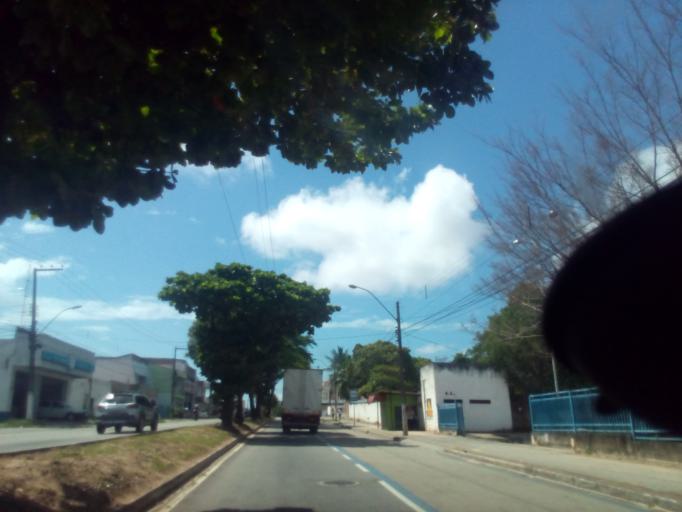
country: BR
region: Rio Grande do Norte
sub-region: Natal
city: Natal
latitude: -5.8220
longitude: -35.2313
